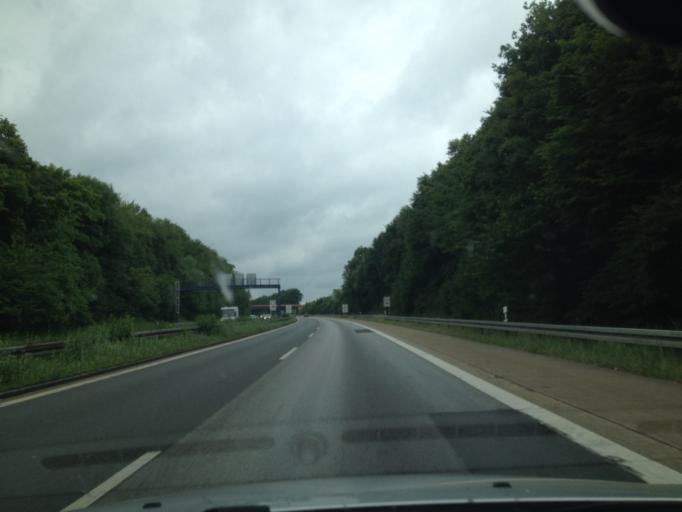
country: DE
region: Bavaria
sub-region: Regierungsbezirk Unterfranken
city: Esselbach
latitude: 49.8304
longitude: 9.5324
